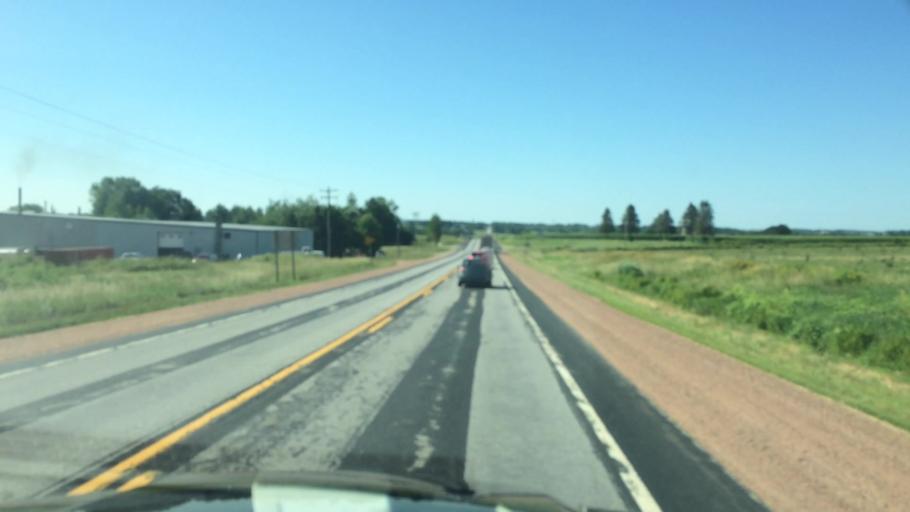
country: US
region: Wisconsin
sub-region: Marathon County
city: Stratford
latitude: 44.8319
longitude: -90.0792
